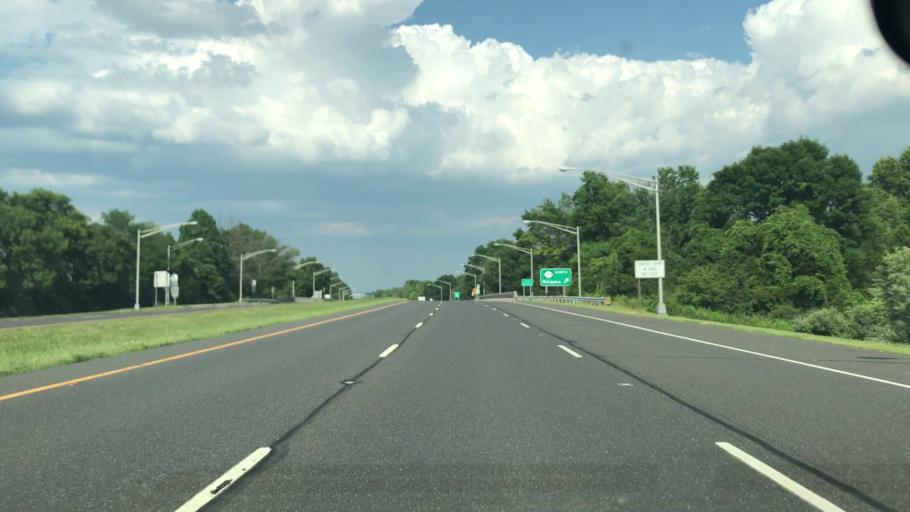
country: US
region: New Jersey
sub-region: Hunterdon County
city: Lambertville
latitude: 40.4176
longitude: -74.8789
